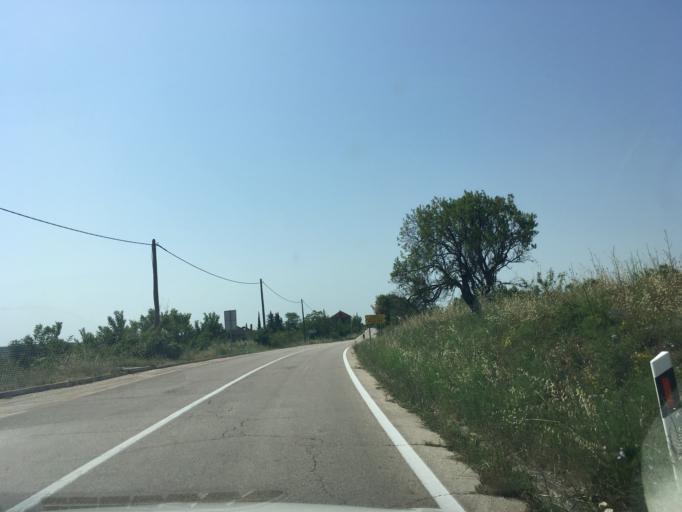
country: HR
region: Zadarska
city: Benkovac
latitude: 43.9984
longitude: 15.6762
